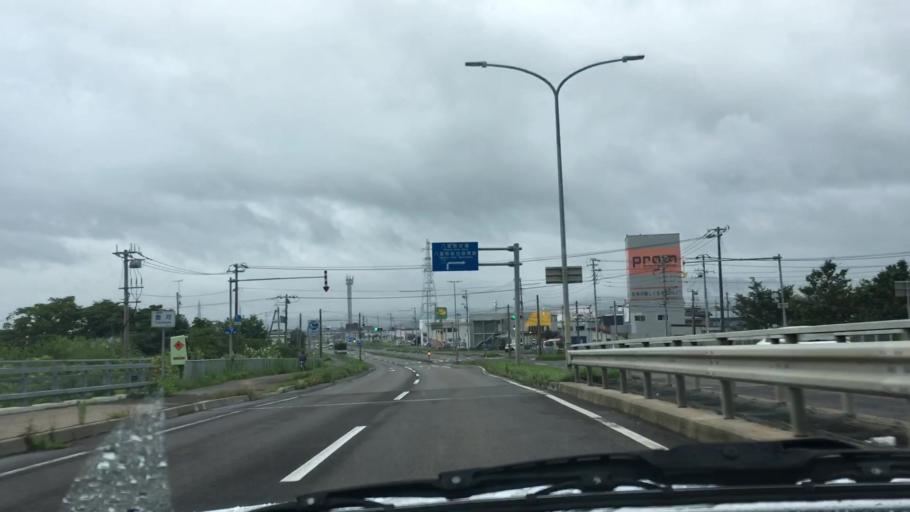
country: JP
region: Hokkaido
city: Nanae
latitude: 42.2622
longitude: 140.2742
